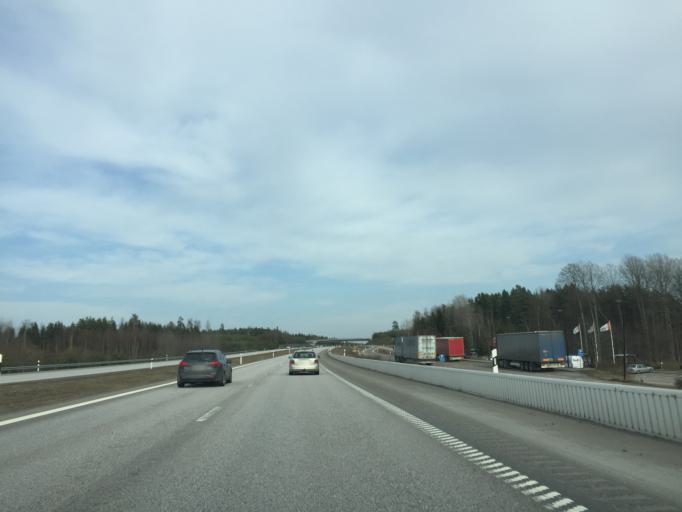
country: SE
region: Vaestmanland
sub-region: Arboga Kommun
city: Arboga
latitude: 59.3983
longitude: 15.7123
